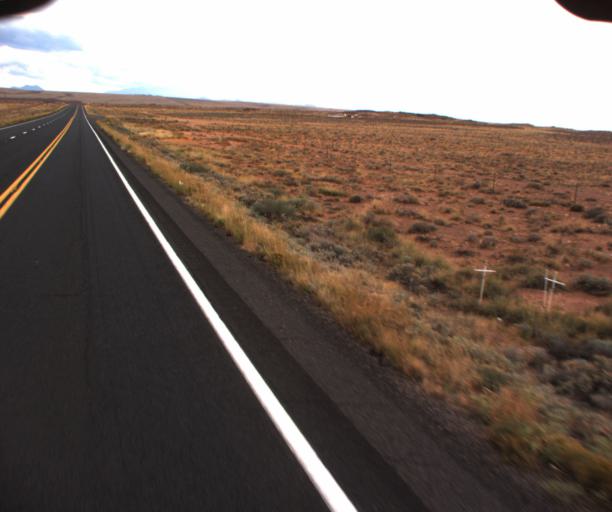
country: US
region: Arizona
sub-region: Coconino County
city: Tuba City
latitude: 35.8062
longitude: -111.4449
